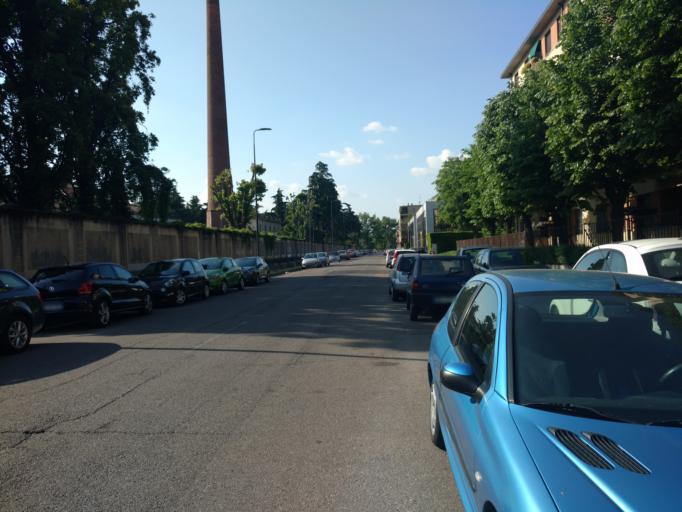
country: IT
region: Lombardy
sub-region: Citta metropolitana di Milano
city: Romano Banco
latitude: 45.4596
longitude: 9.1257
